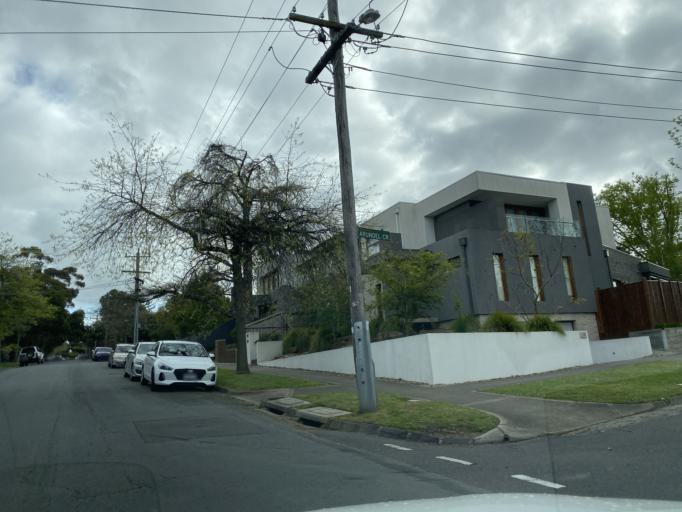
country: AU
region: Victoria
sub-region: Boroondara
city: Canterbury
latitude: -37.8326
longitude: 145.0915
